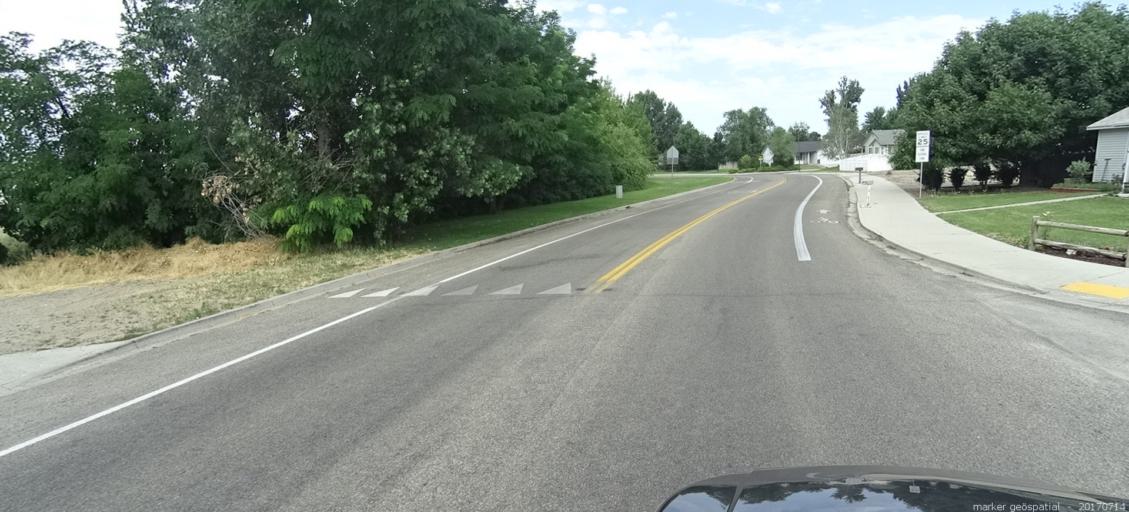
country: US
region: Idaho
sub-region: Ada County
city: Kuna
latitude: 43.4921
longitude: -116.4277
